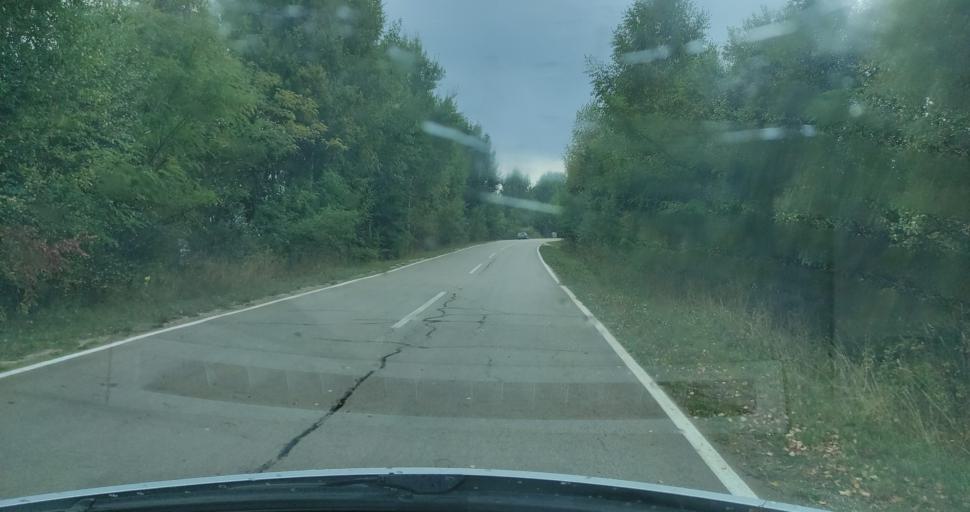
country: RS
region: Central Serbia
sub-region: Jablanicki Okrug
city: Crna Trava
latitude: 42.7088
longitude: 22.3281
